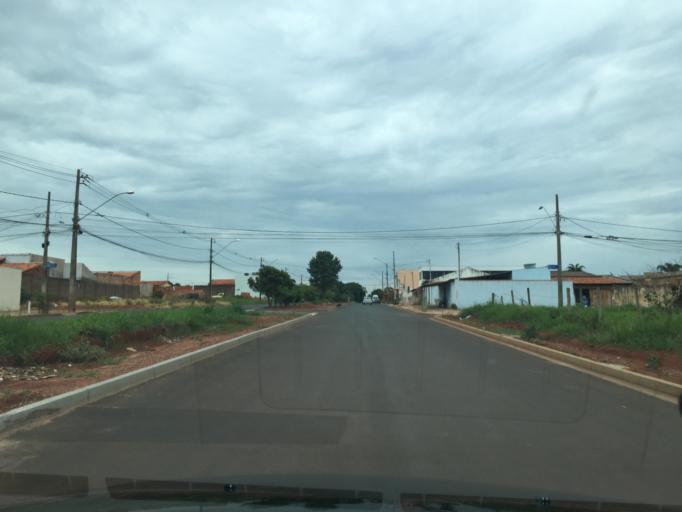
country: BR
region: Minas Gerais
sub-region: Uberlandia
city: Uberlandia
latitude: -18.8713
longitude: -48.2250
